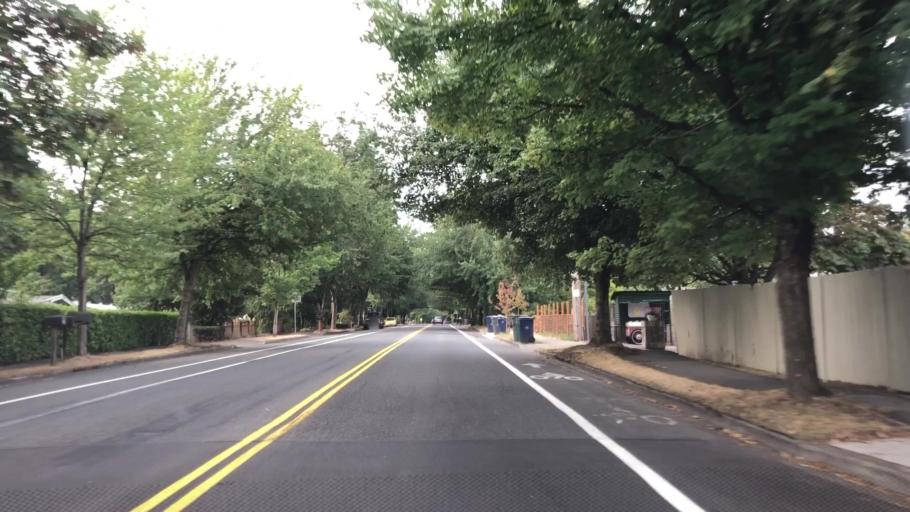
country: US
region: Washington
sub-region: King County
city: Redmond
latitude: 47.6754
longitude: -122.1639
